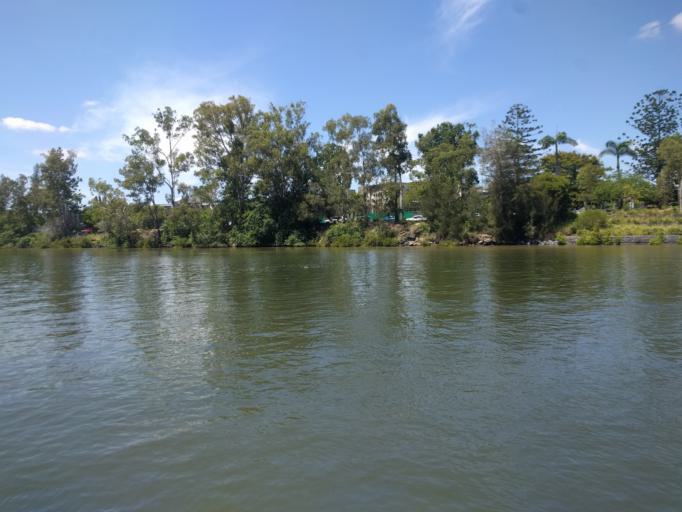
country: AU
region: Queensland
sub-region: Brisbane
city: South Brisbane
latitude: -27.4919
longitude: 153.0152
